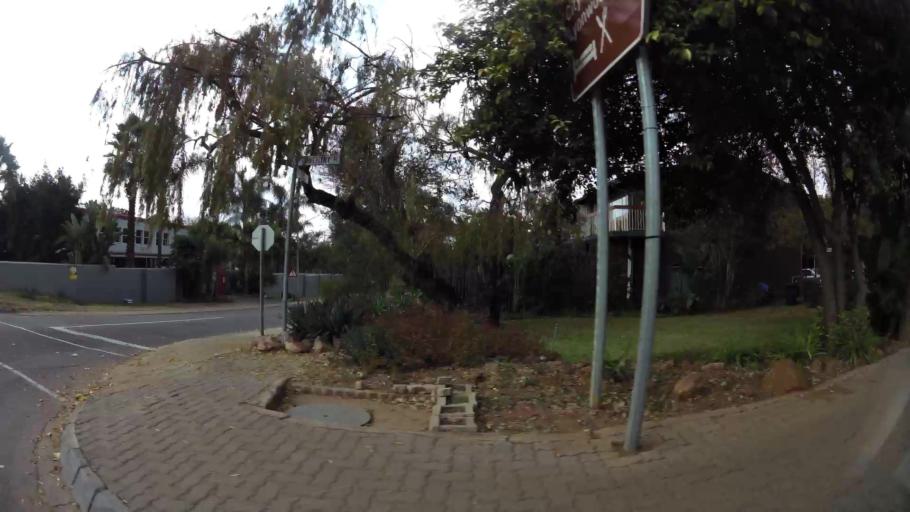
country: ZA
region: Gauteng
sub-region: City of Tshwane Metropolitan Municipality
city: Pretoria
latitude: -25.7643
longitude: 28.2798
